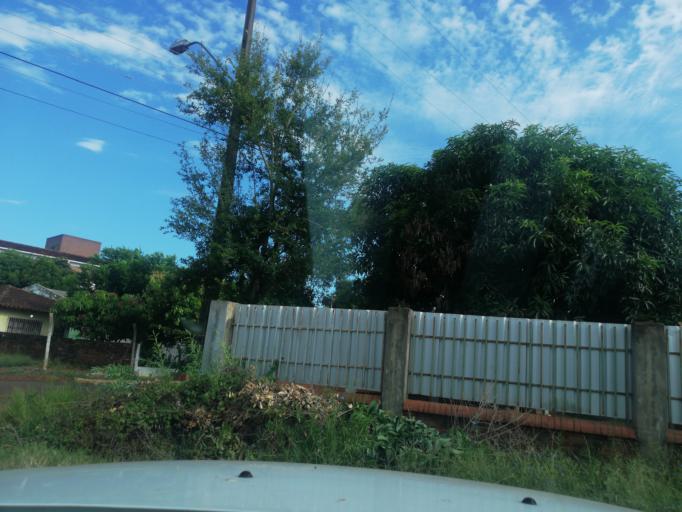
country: PY
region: Itapua
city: Encarnacion
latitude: -27.3436
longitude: -55.8478
